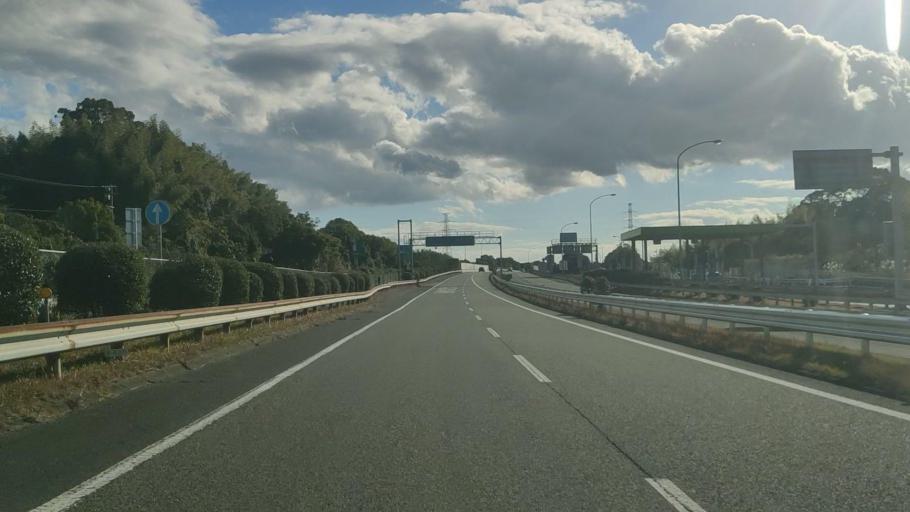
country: JP
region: Fukuoka
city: Nogata
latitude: 33.7869
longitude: 130.7461
